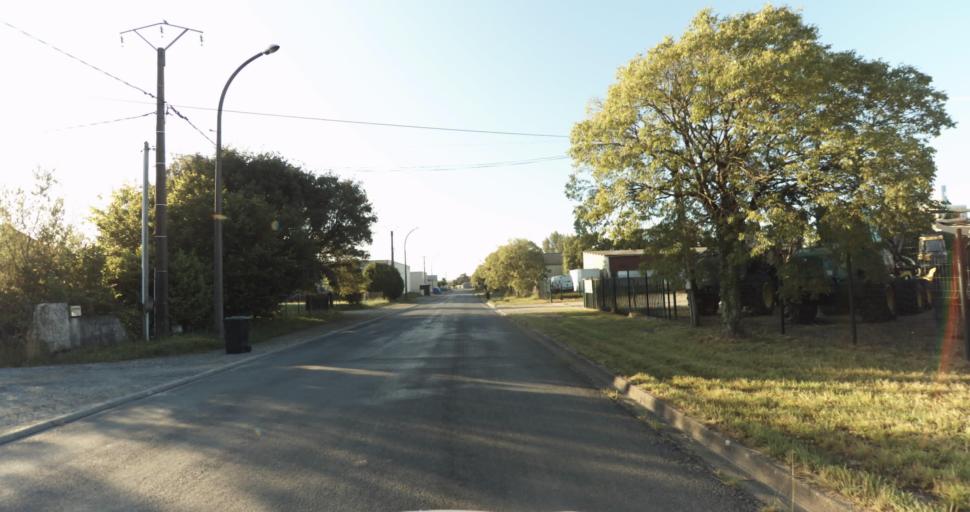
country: FR
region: Aquitaine
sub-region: Departement de la Gironde
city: Bazas
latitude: 44.4388
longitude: -0.2310
